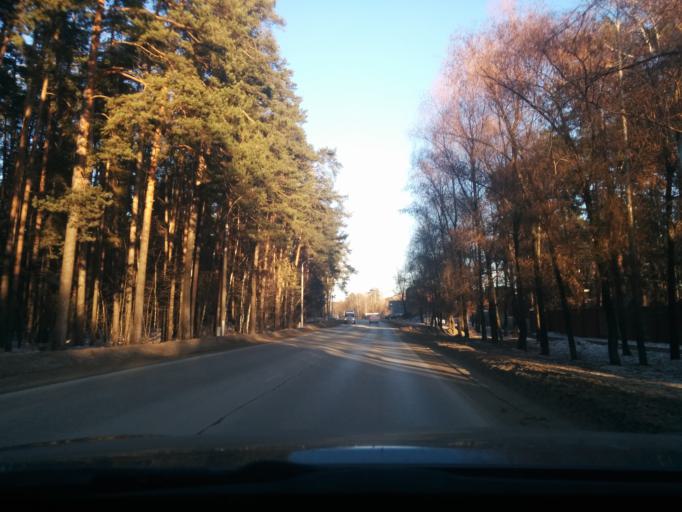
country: RU
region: Perm
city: Kultayevo
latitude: 58.0089
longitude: 55.9761
